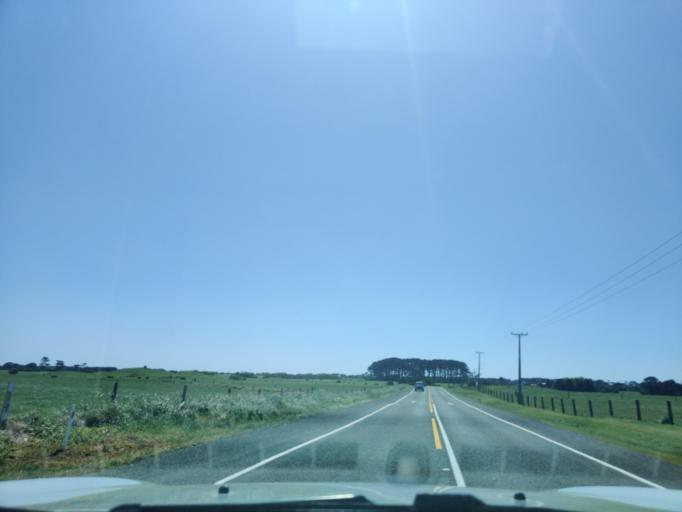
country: NZ
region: Taranaki
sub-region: South Taranaki District
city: Opunake
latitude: -39.3850
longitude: 173.8118
